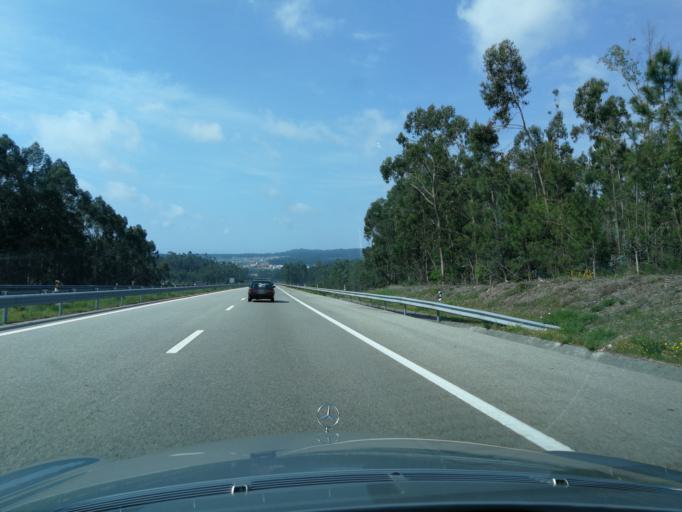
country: PT
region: Porto
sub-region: Vila do Conde
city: Arvore
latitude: 41.3820
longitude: -8.6637
